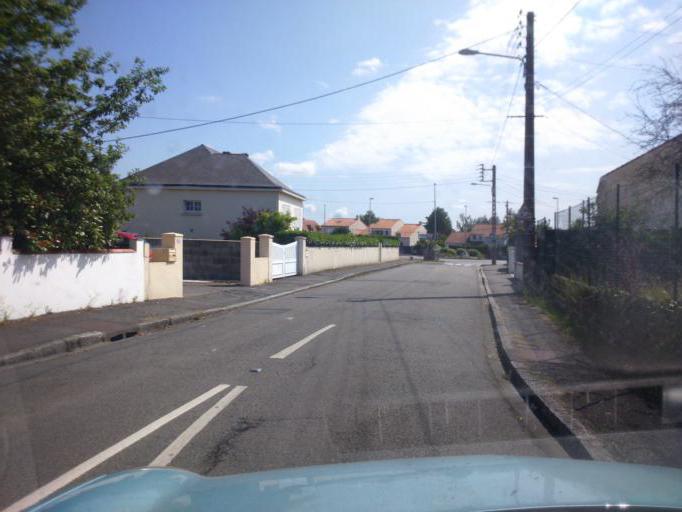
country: FR
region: Pays de la Loire
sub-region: Departement de la Loire-Atlantique
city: Saint-Sebastien-sur-Loire
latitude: 47.1995
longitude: -1.5148
